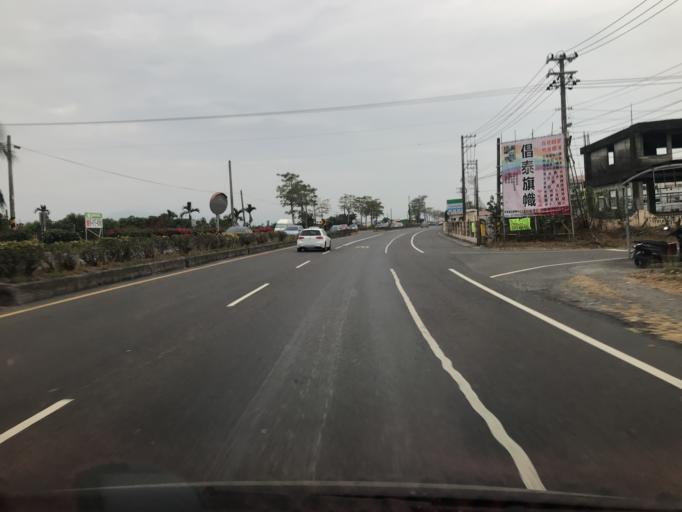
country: TW
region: Taiwan
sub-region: Pingtung
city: Pingtung
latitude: 22.4202
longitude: 120.5829
